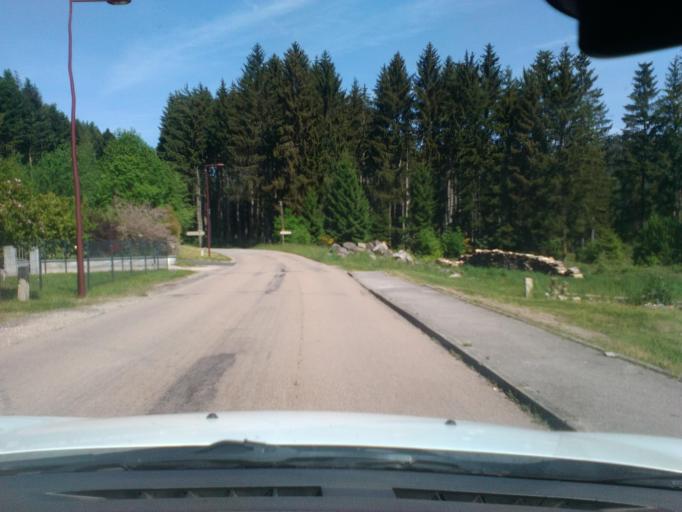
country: FR
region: Lorraine
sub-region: Departement des Vosges
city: Bruyeres
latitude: 48.2428
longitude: 6.7316
